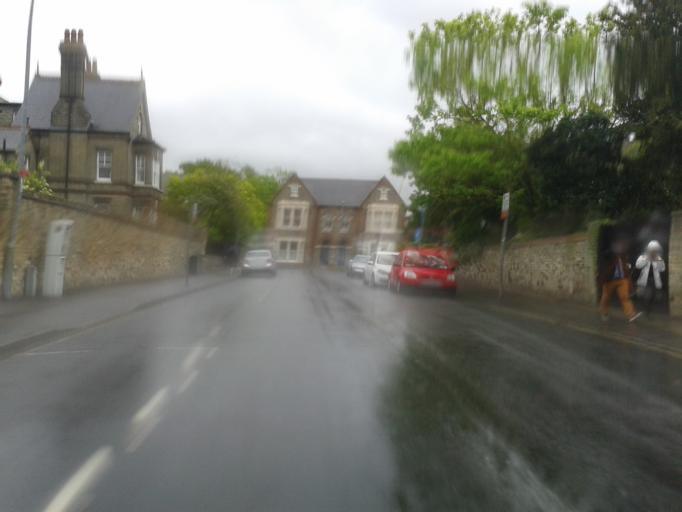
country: GB
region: England
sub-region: Cambridgeshire
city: Cambridge
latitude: 52.1984
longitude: 0.1321
